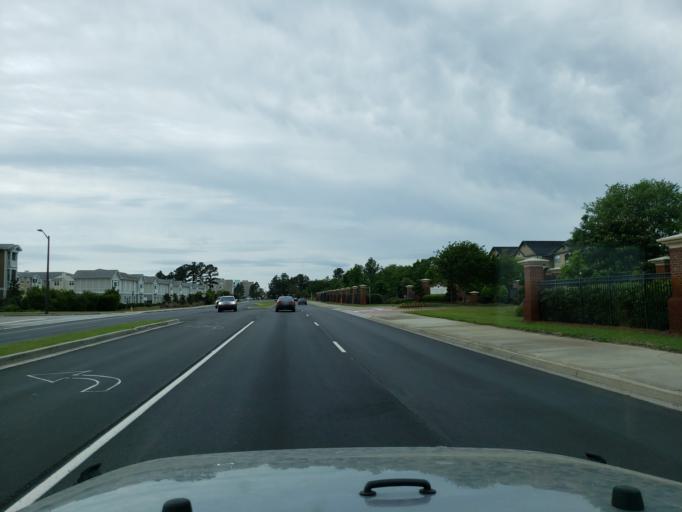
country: US
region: Georgia
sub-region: Chatham County
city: Pooler
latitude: 32.1497
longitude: -81.2457
